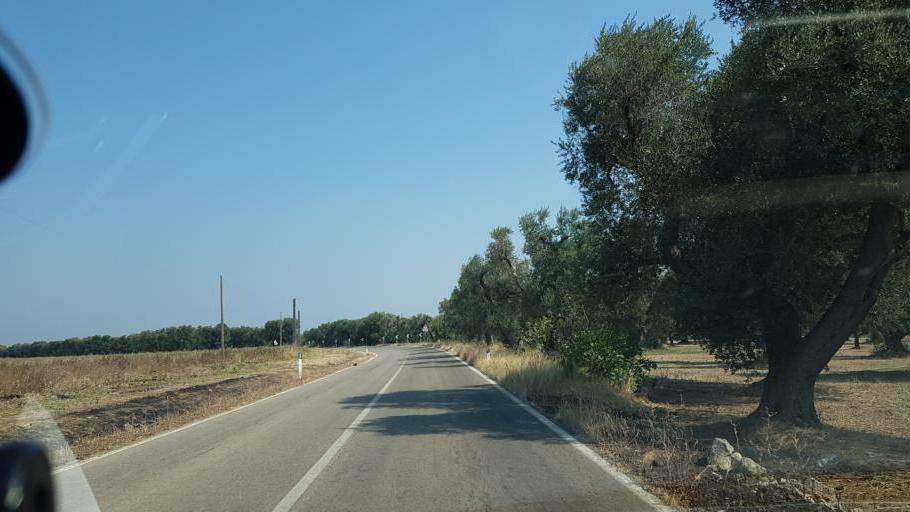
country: IT
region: Apulia
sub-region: Provincia di Brindisi
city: Torre Santa Susanna
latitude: 40.4944
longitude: 17.6955
